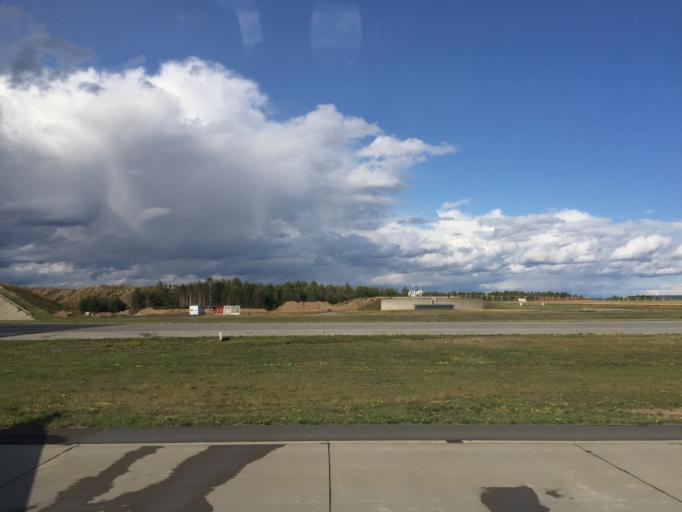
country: NO
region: Akershus
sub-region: Ullensaker
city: Jessheim
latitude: 60.2009
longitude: 11.1180
